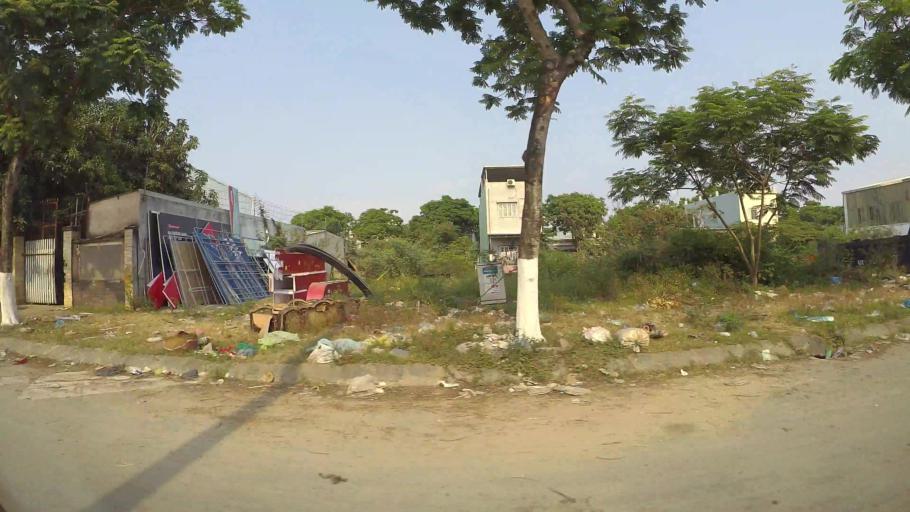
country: VN
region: Da Nang
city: Thanh Khe
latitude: 16.0510
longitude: 108.1742
